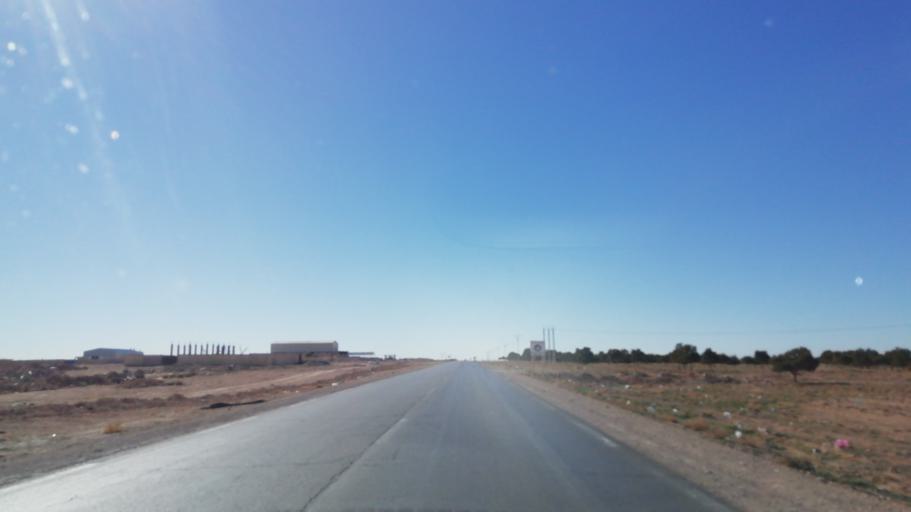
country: DZ
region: Saida
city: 'Ain el Hadjar
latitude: 34.0329
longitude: 0.0752
